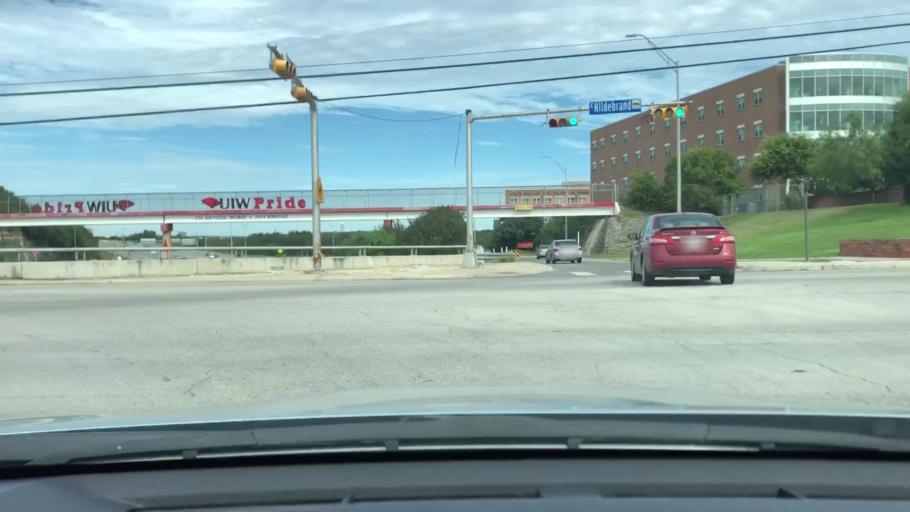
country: US
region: Texas
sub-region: Bexar County
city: Olmos Park
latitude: 29.4655
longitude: -98.4734
